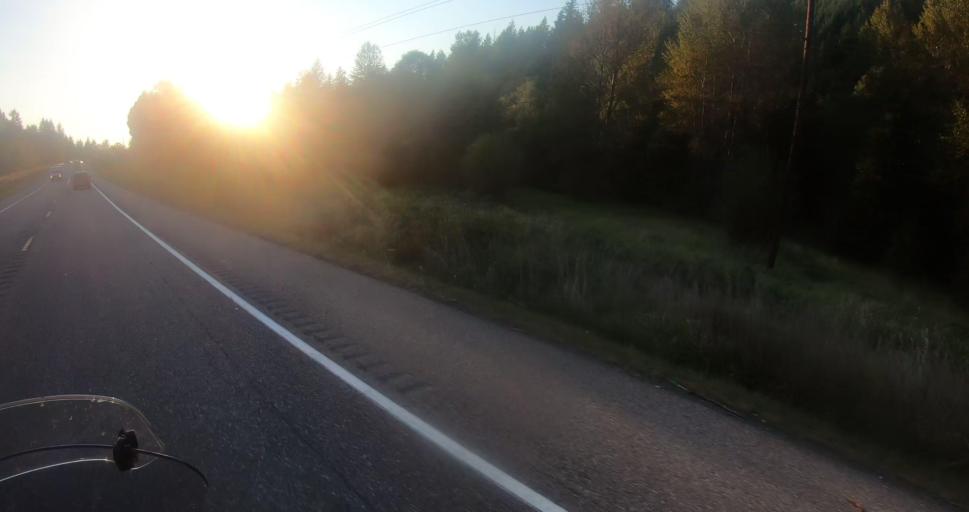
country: US
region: Washington
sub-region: Lewis County
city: Morton
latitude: 46.5434
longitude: -122.0908
